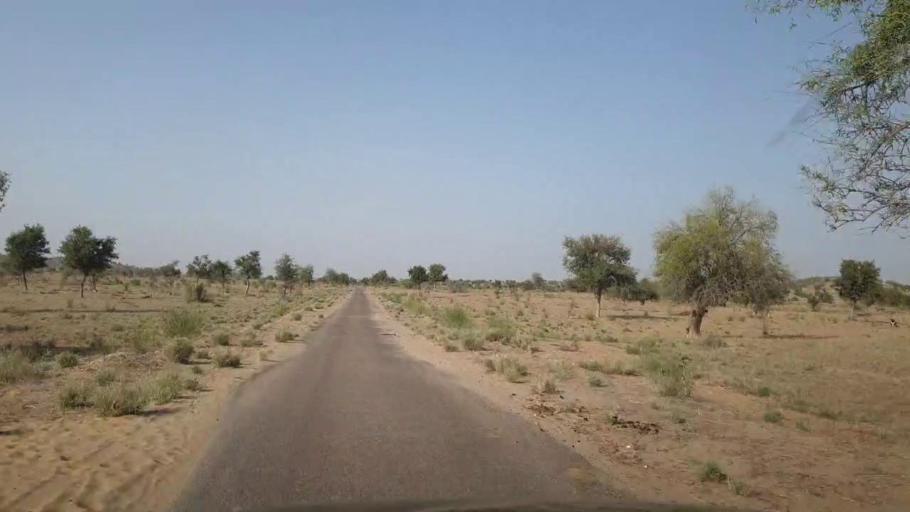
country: PK
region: Sindh
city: Islamkot
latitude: 25.1334
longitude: 70.5173
